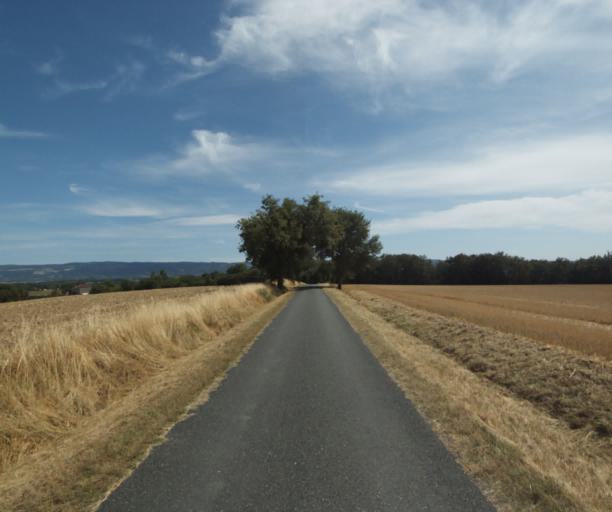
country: FR
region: Midi-Pyrenees
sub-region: Departement du Tarn
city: Puylaurens
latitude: 43.5283
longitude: 2.0227
